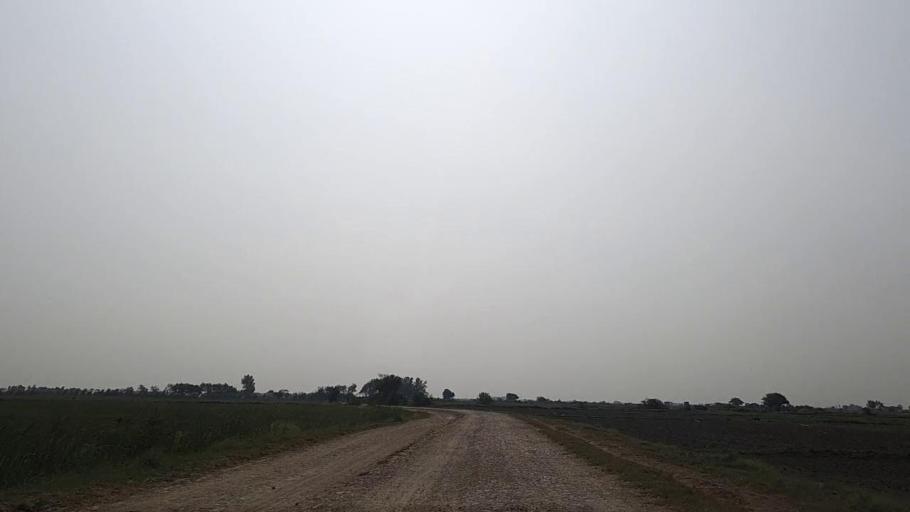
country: PK
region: Sindh
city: Mirpur Sakro
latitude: 24.6381
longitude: 67.7674
